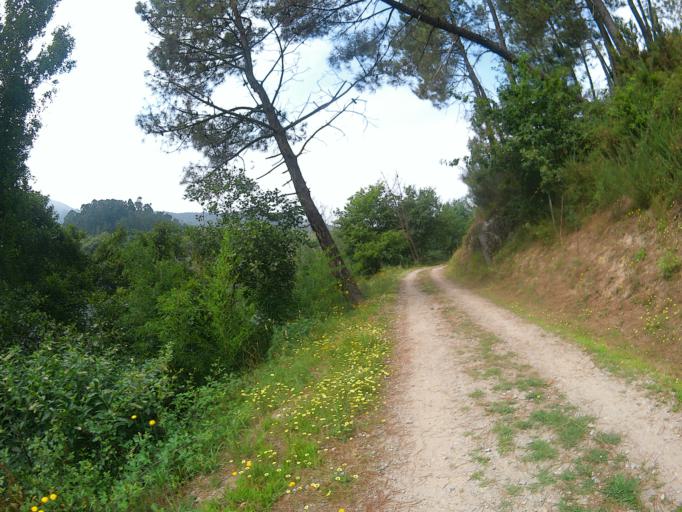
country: PT
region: Viana do Castelo
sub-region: Ponte de Lima
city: Ponte de Lima
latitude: 41.7825
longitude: -8.5369
